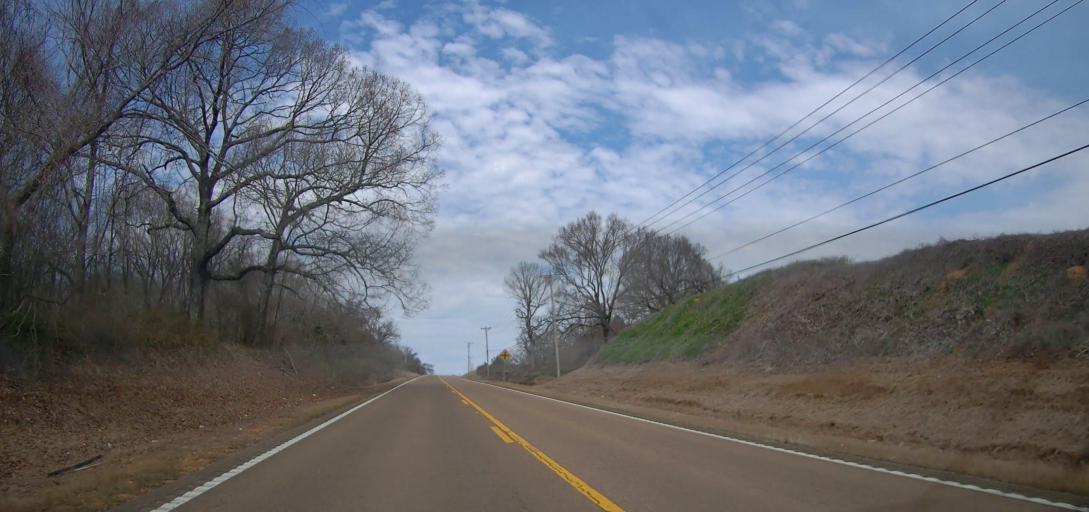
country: US
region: Mississippi
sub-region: Marshall County
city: Holly Springs
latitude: 34.7353
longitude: -89.4223
